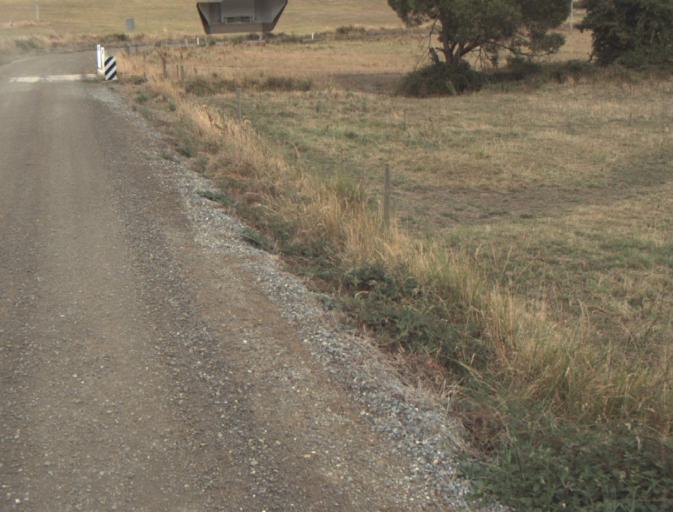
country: AU
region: Tasmania
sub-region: Launceston
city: Mayfield
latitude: -41.2130
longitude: 147.1485
